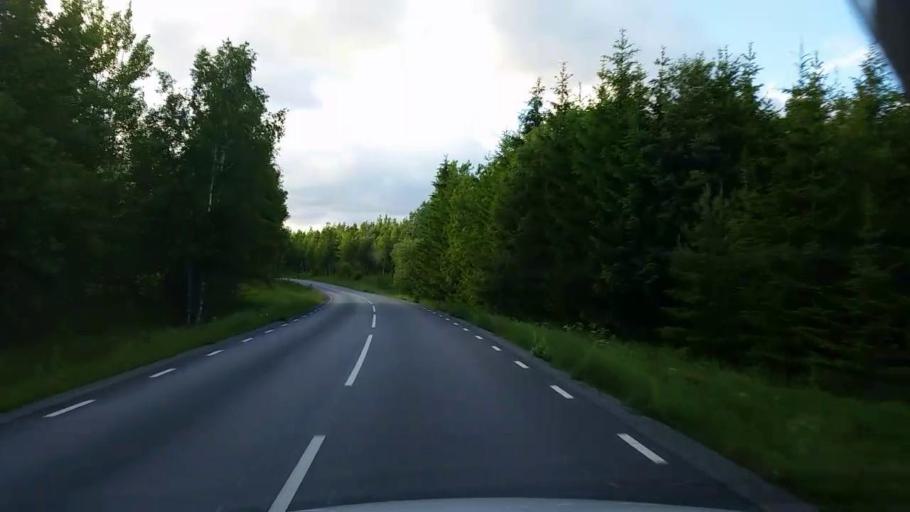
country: SE
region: Vaestmanland
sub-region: Kopings Kommun
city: Kolsva
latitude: 59.6773
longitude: 15.8416
